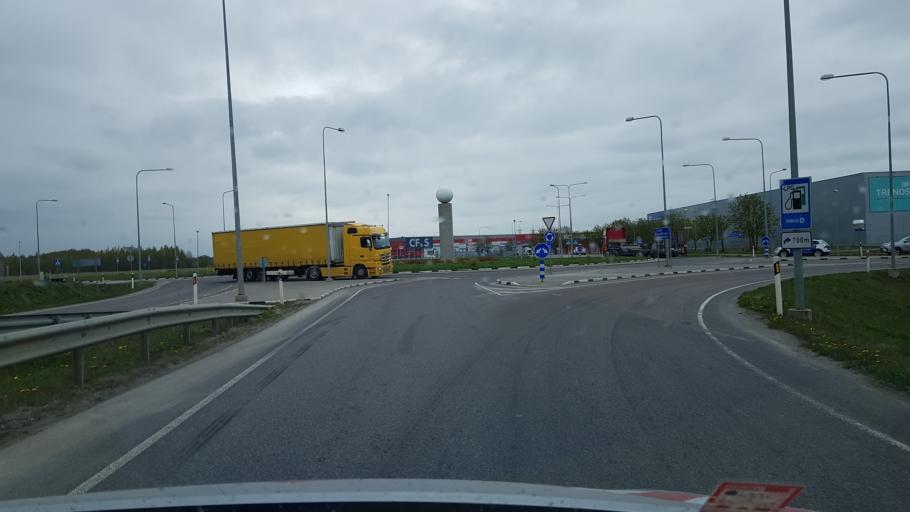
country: EE
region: Harju
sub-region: Joelaehtme vald
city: Loo
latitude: 59.4462
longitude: 24.9296
